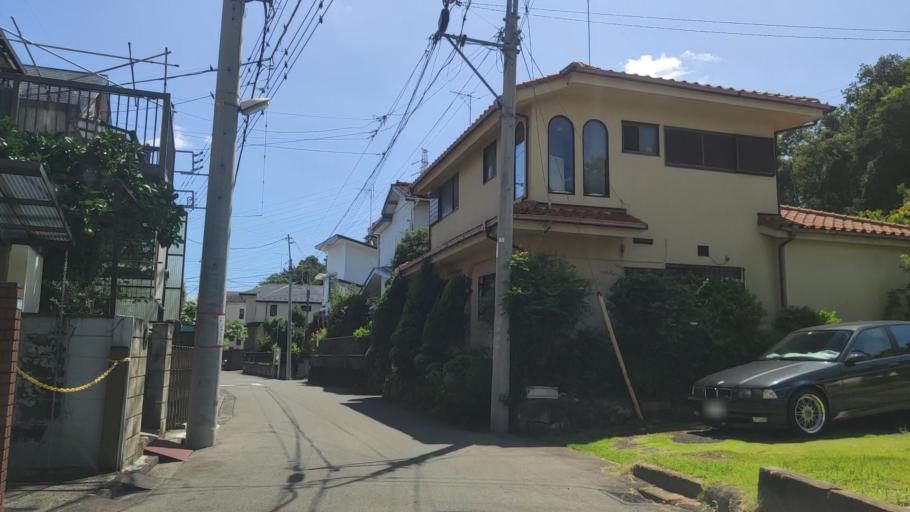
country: JP
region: Kanagawa
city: Yokohama
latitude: 35.5321
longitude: 139.6243
